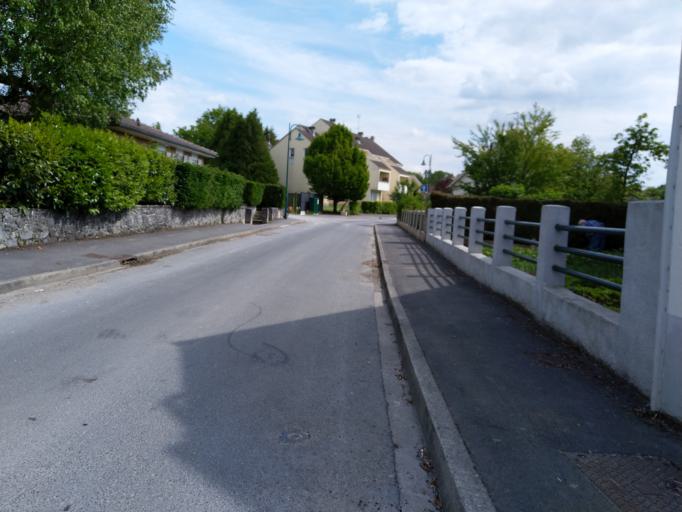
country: FR
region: Picardie
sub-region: Departement de l'Aisne
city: Boue
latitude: 50.0108
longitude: 3.6956
